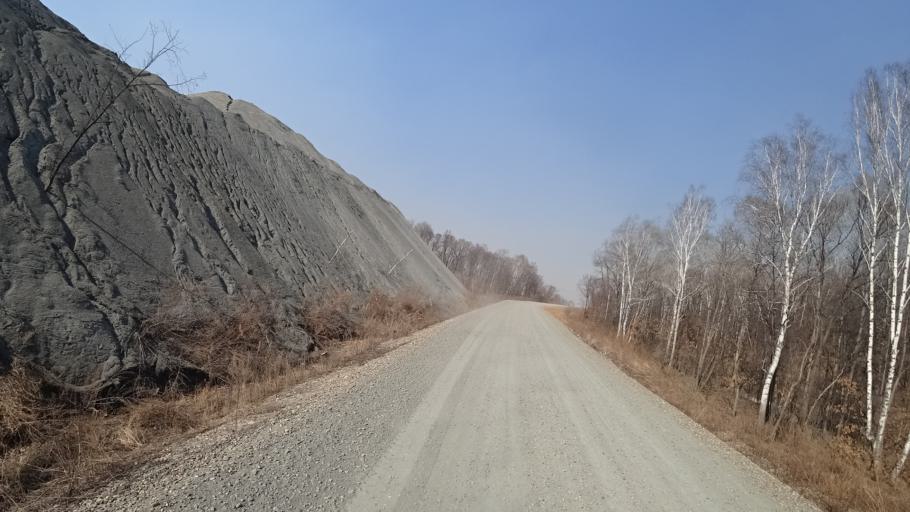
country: RU
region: Amur
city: Novobureyskiy
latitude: 49.7986
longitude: 129.9582
